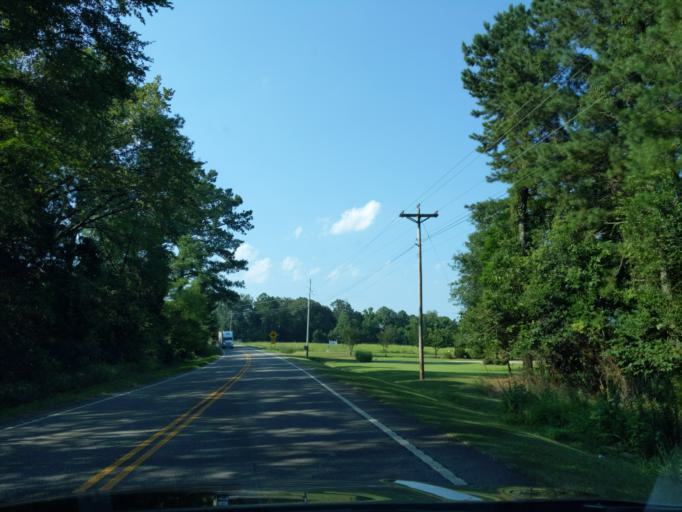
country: US
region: South Carolina
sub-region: Newberry County
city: Prosperity
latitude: 34.0642
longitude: -81.5610
